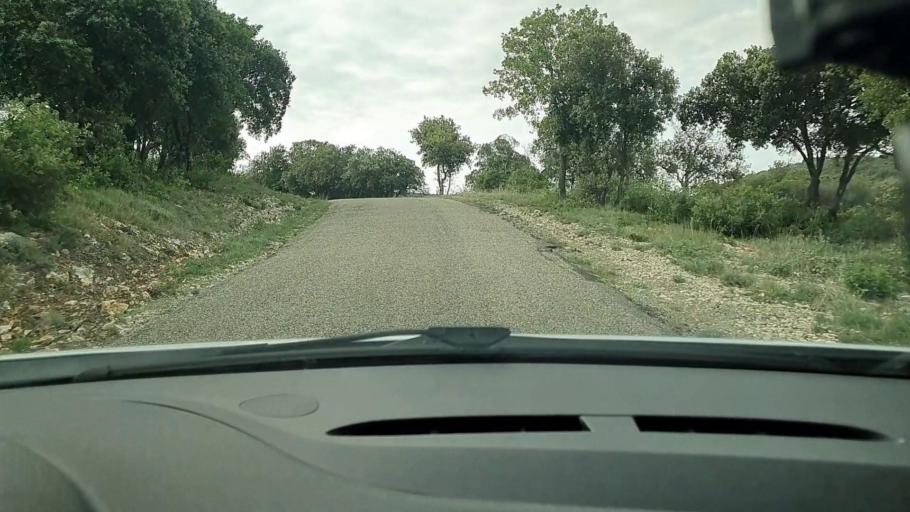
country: FR
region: Languedoc-Roussillon
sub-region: Departement du Gard
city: Montaren-et-Saint-Mediers
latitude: 44.0963
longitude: 4.3189
